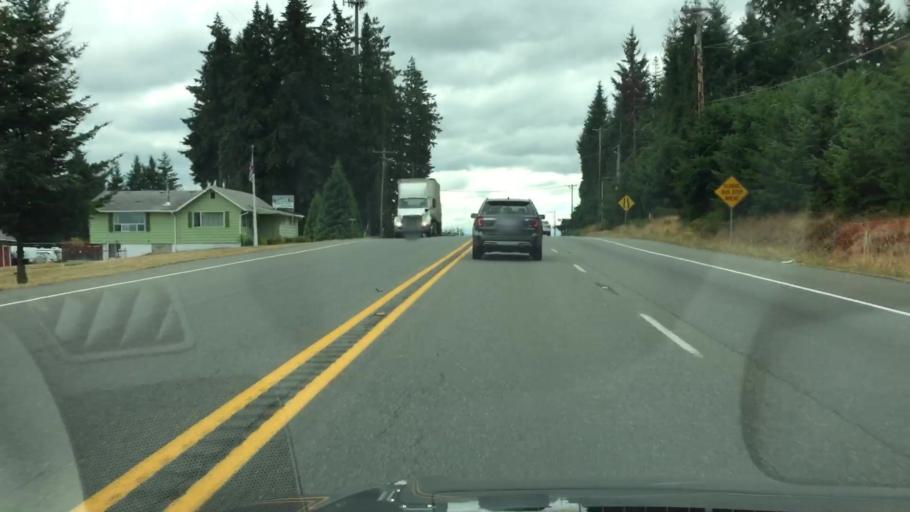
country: US
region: Washington
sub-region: Pierce County
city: Graham
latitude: 47.0296
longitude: -122.2960
